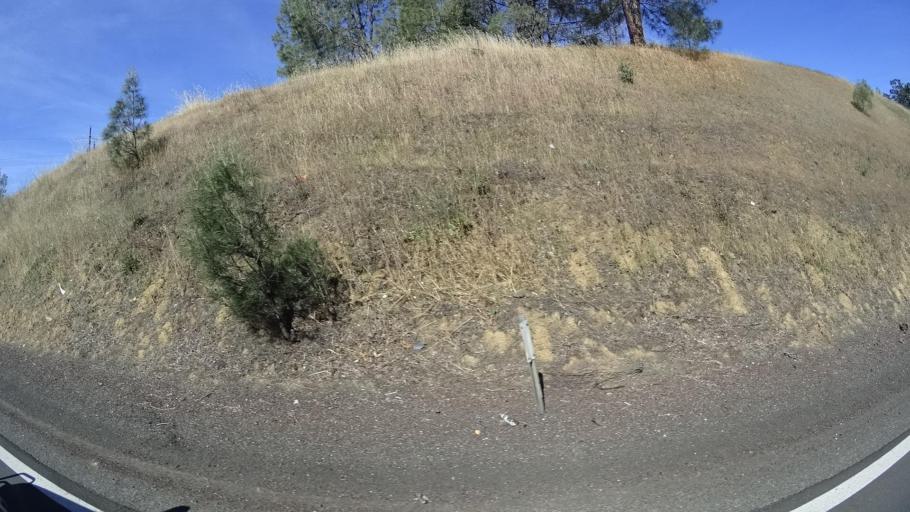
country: US
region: California
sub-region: Lake County
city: Kelseyville
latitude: 38.9573
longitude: -122.8278
